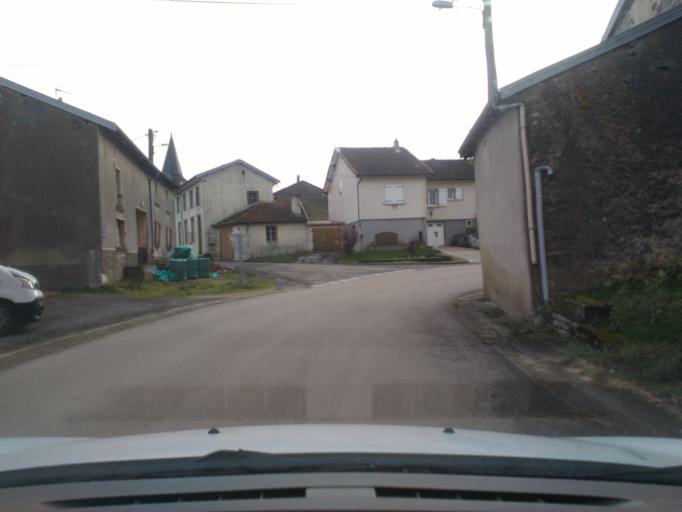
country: FR
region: Lorraine
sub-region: Departement des Vosges
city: Vittel
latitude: 48.3260
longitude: 5.9853
